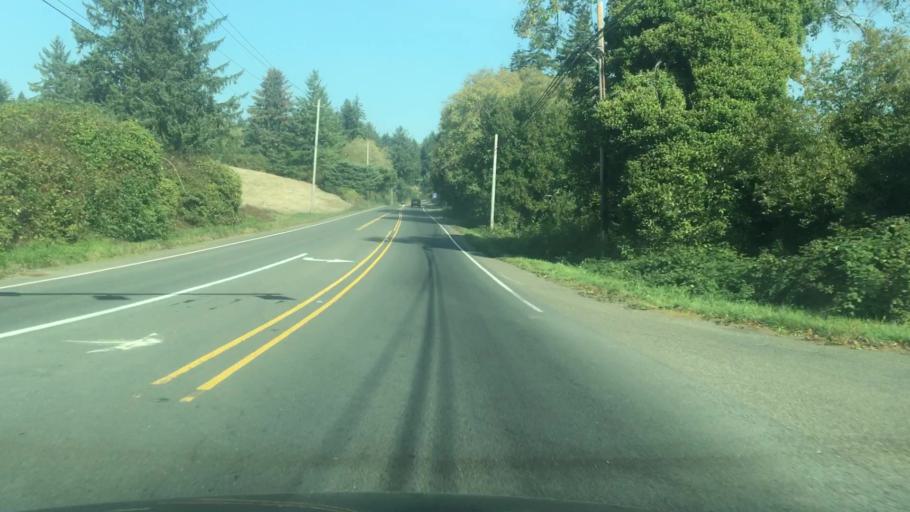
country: US
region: Oregon
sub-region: Lincoln County
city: Lincoln City
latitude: 45.0017
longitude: -123.9868
